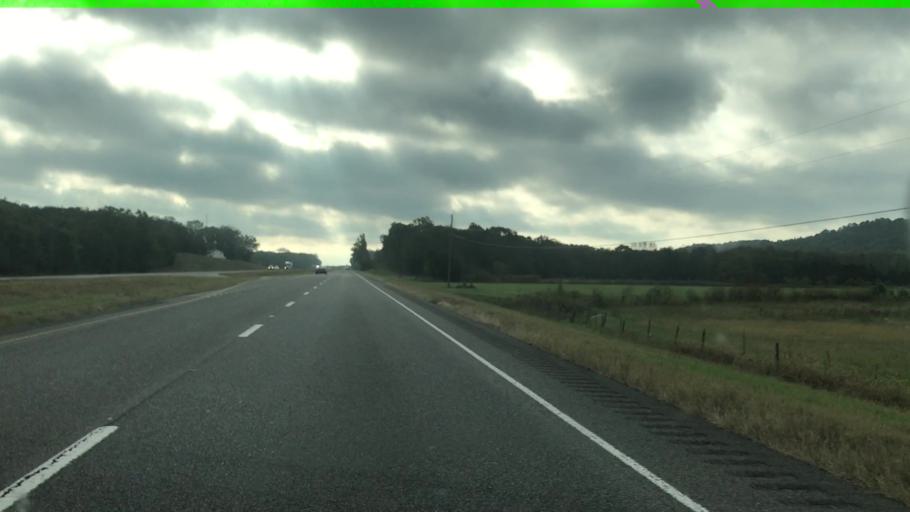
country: US
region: Alabama
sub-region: Morgan County
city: Danville
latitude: 34.4052
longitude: -87.1407
